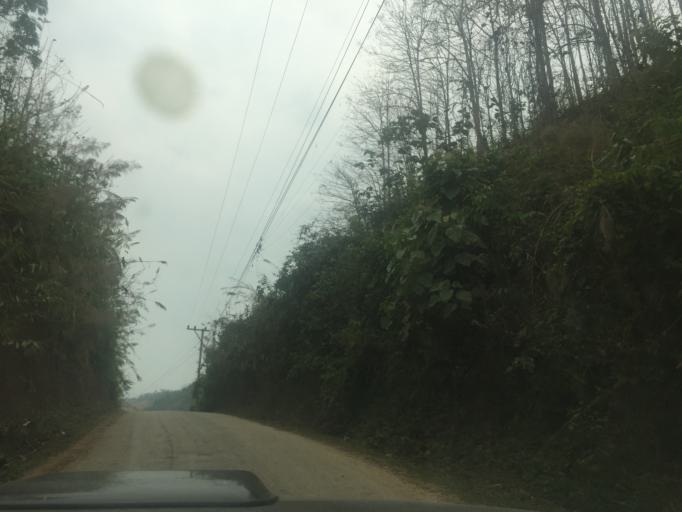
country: LA
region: Vientiane
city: Muang Sanakham
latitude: 18.3839
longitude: 101.5387
